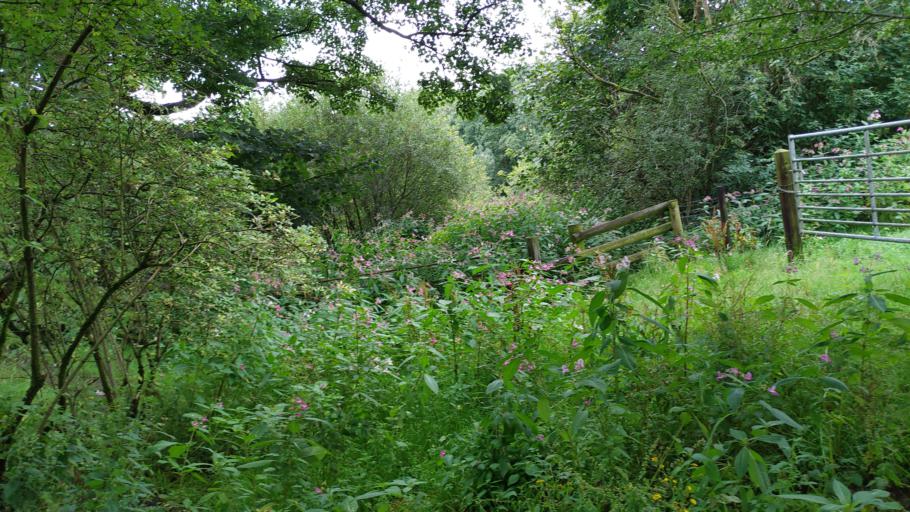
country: GB
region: England
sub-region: Lancashire
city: Coppull
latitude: 53.6337
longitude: -2.6584
